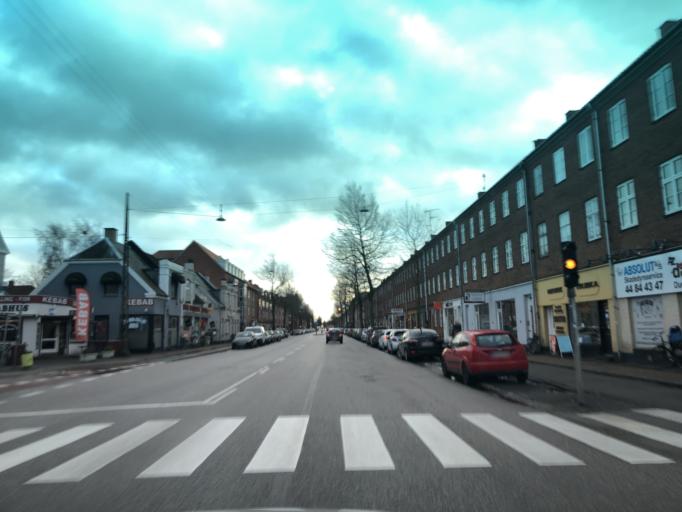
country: DK
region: Capital Region
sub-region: Tarnby Kommune
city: Tarnby
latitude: 55.6497
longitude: 12.6128
